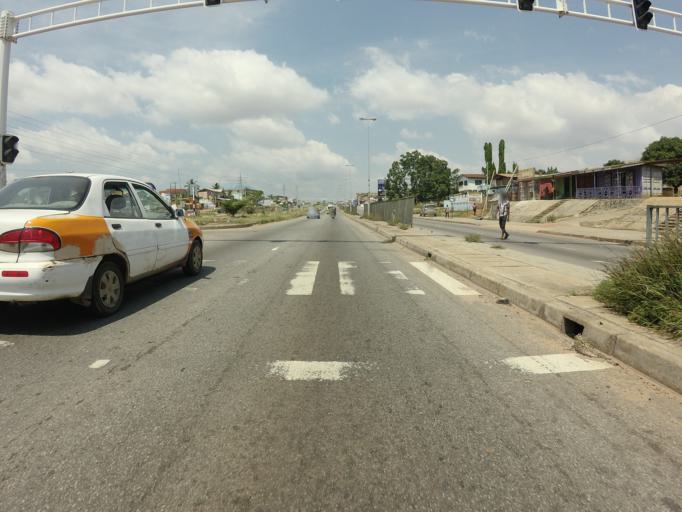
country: GH
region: Greater Accra
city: Gbawe
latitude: 5.5952
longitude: -0.2893
